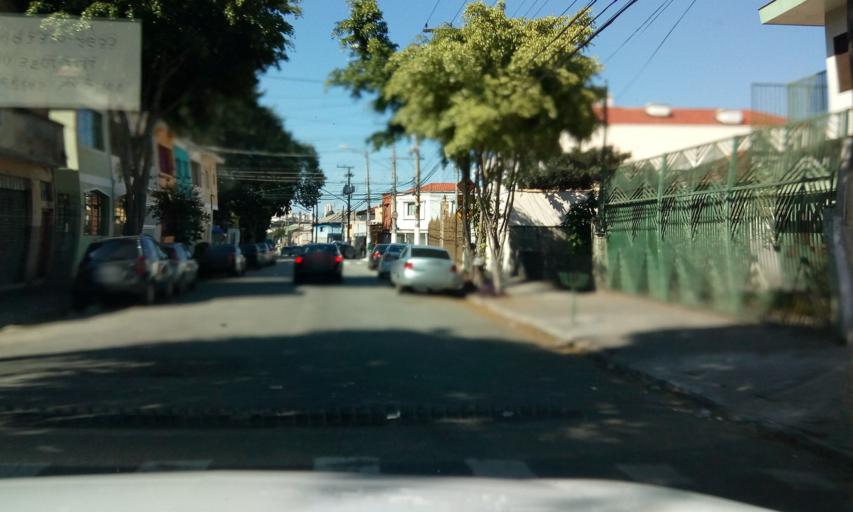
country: BR
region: Sao Paulo
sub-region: Guarulhos
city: Guarulhos
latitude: -23.5344
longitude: -46.5576
